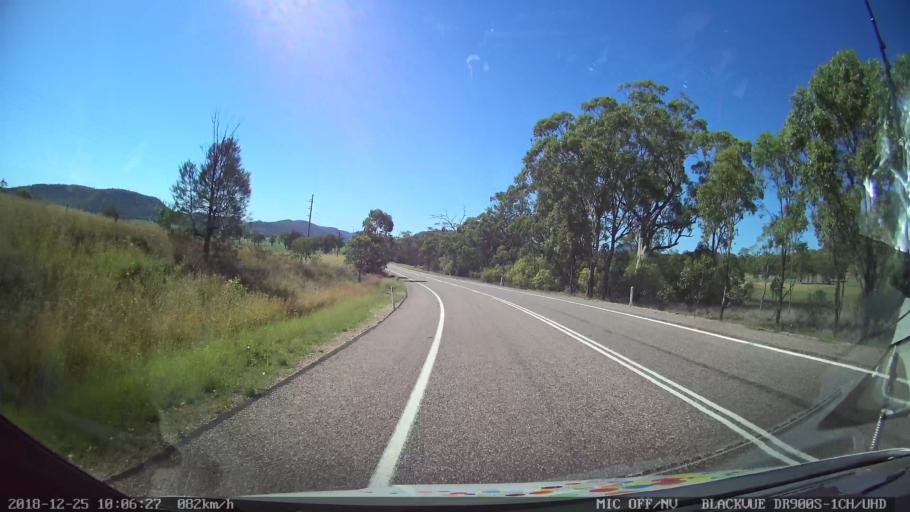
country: AU
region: New South Wales
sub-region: Upper Hunter Shire
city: Merriwa
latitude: -32.2600
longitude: 150.4898
